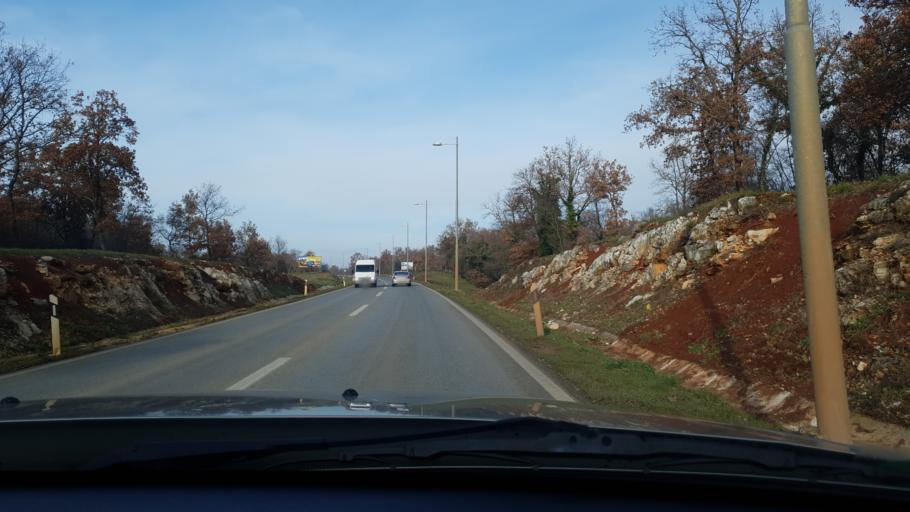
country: HR
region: Istarska
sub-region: Grad Porec
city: Porec
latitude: 45.2441
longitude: 13.6252
